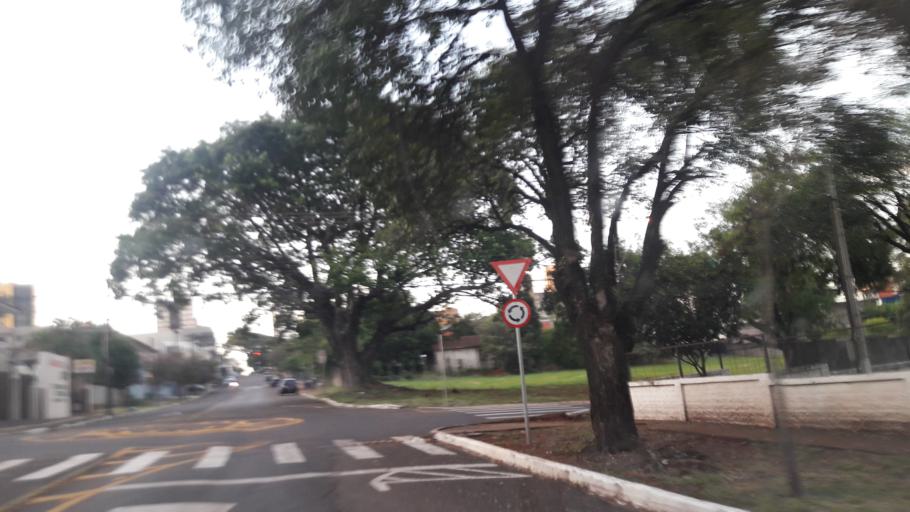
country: BR
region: Parana
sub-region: Cascavel
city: Cascavel
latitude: -24.9558
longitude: -53.4498
